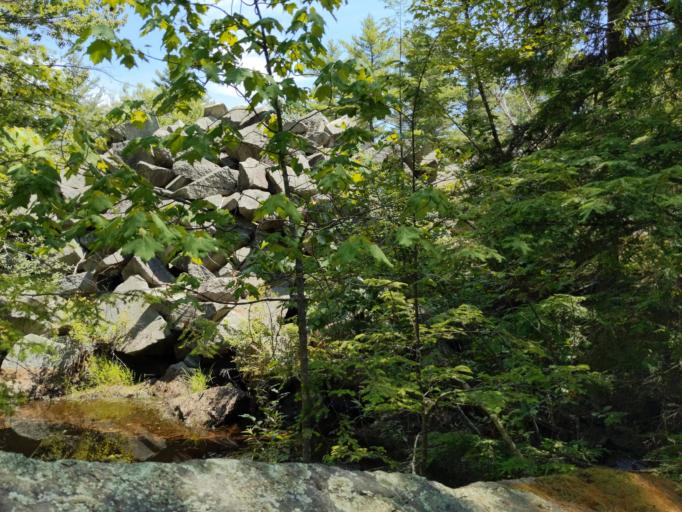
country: US
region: New Hampshire
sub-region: Grafton County
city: Lebanon
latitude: 43.6581
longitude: -72.2589
